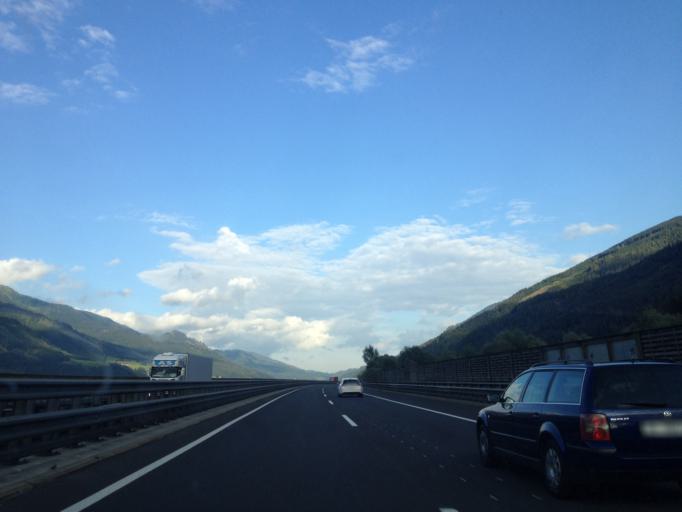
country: AT
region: Styria
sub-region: Politischer Bezirk Liezen
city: Trieben
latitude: 47.4865
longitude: 14.5246
